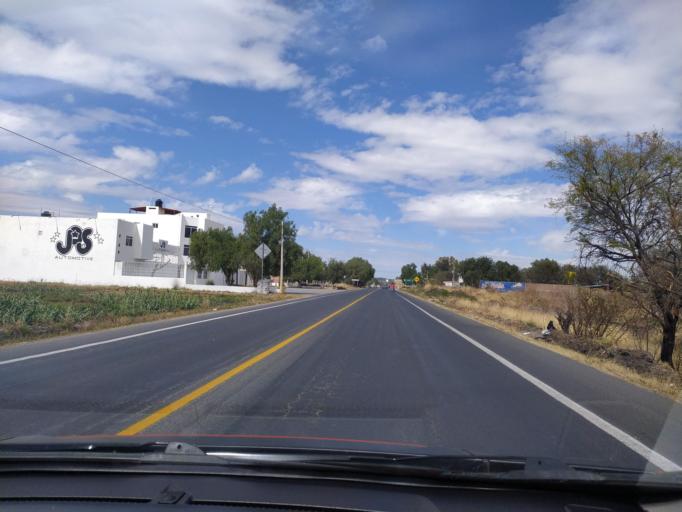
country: LA
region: Oudomxai
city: Muang La
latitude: 21.0133
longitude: 101.8281
